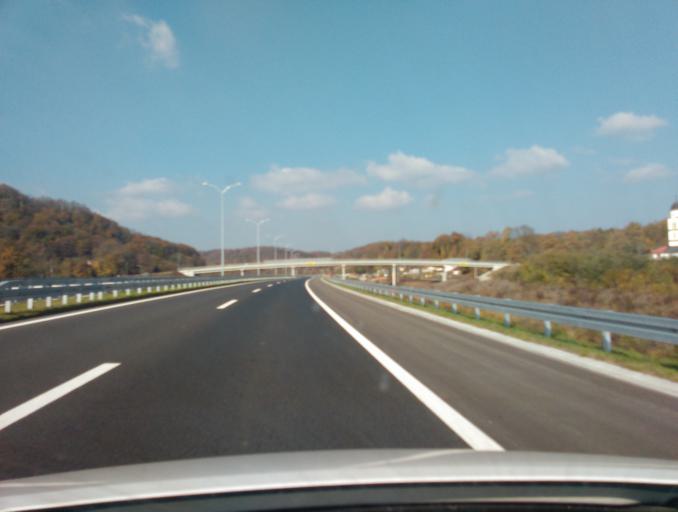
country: BA
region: Republika Srpska
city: Prnjavor
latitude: 44.8891
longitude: 17.6102
